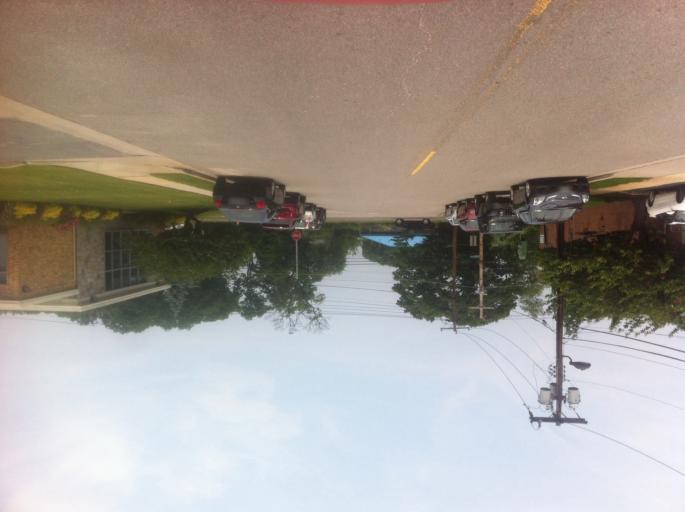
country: US
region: New York
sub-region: Nassau County
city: Massapequa
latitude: 40.6746
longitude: -73.4778
